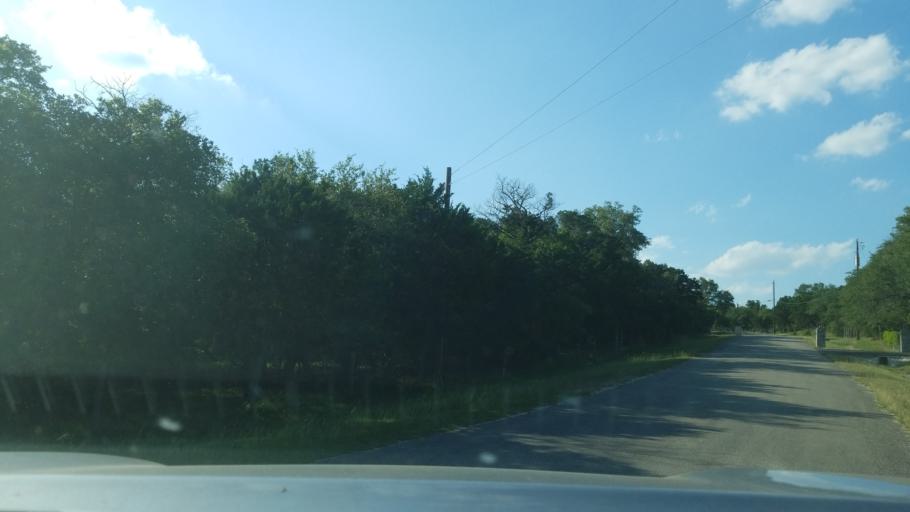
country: US
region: Texas
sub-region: Comal County
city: Bulverde
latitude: 29.7894
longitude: -98.4279
